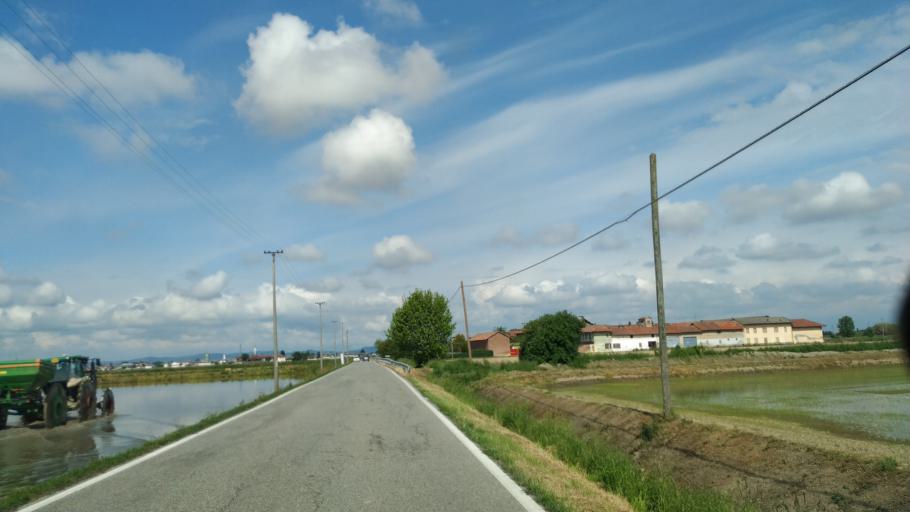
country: IT
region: Piedmont
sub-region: Provincia di Vercelli
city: Crova
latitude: 45.3348
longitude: 8.2003
